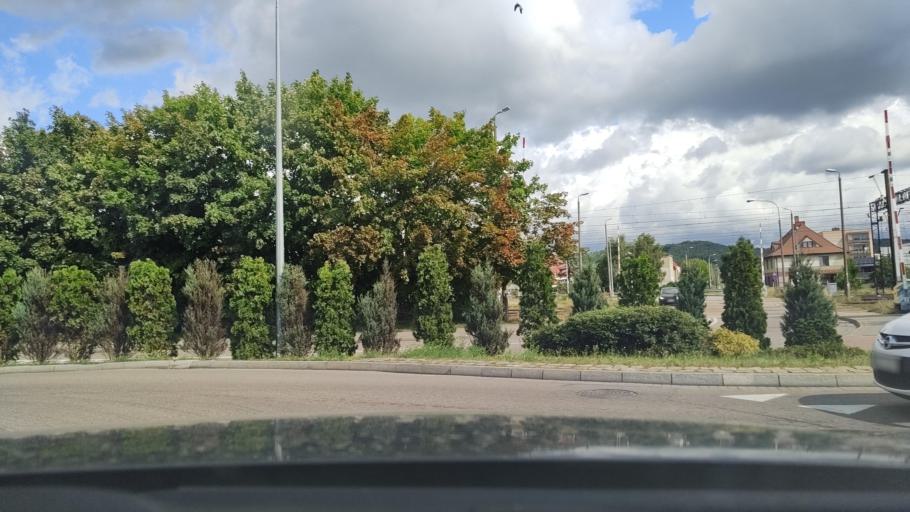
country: PL
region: Pomeranian Voivodeship
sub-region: Powiat wejherowski
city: Wejherowo
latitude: 54.6047
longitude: 18.2350
